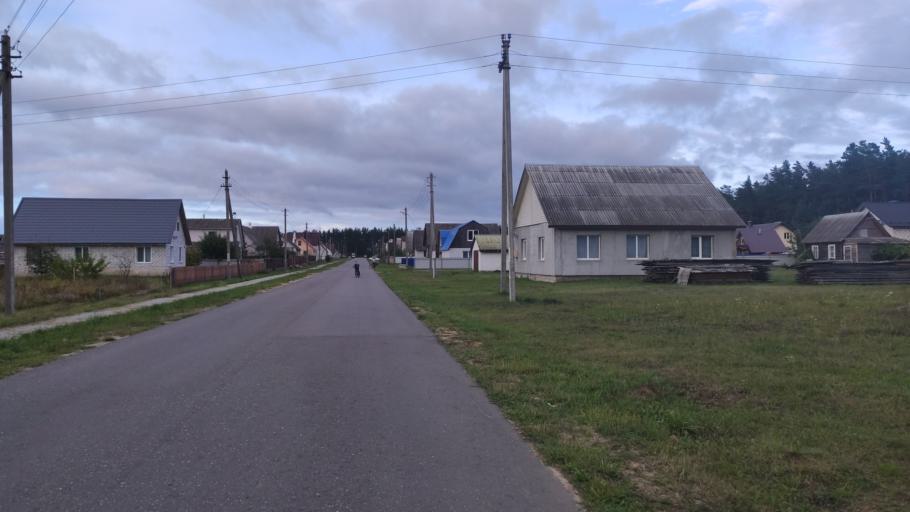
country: BY
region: Minsk
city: Narach
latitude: 54.9272
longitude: 26.6948
